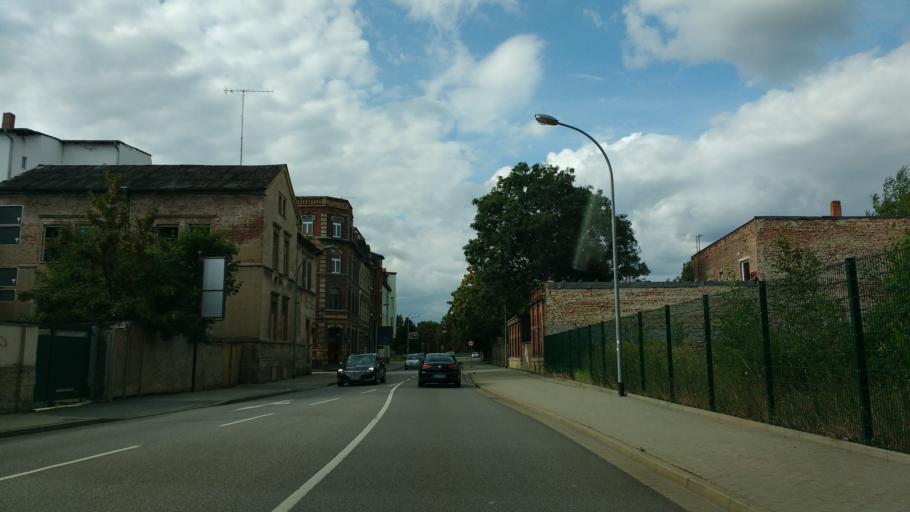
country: DE
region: Saxony-Anhalt
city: Zeitz
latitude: 51.0533
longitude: 12.1284
